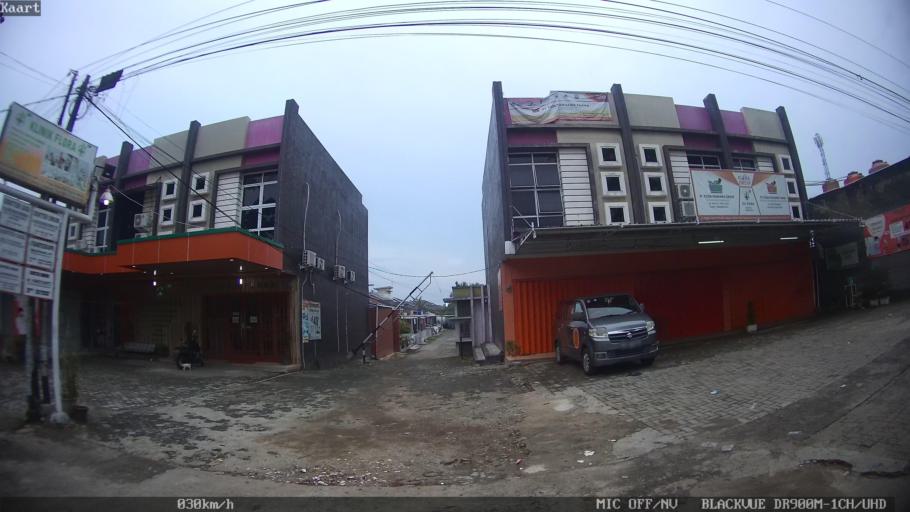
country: ID
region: Lampung
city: Kedaton
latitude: -5.3860
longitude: 105.2477
